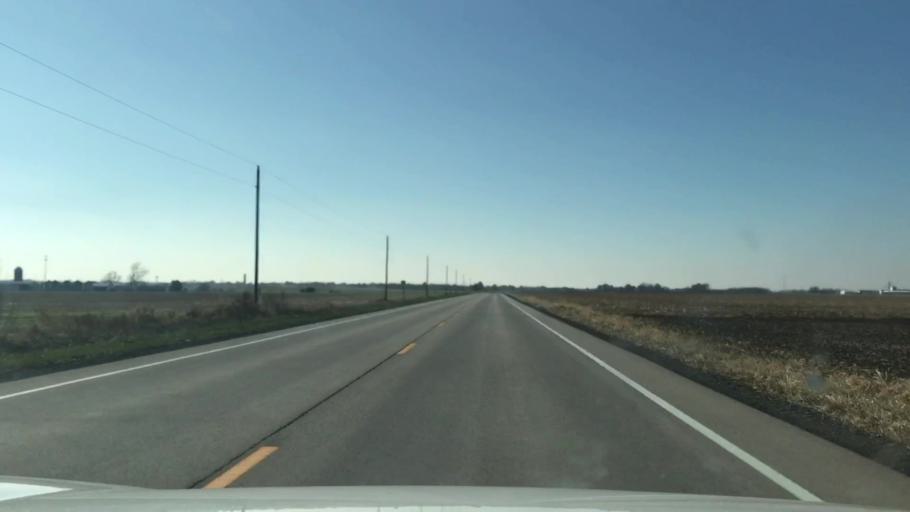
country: US
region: Illinois
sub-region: Washington County
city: Okawville
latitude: 38.4426
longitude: -89.5135
